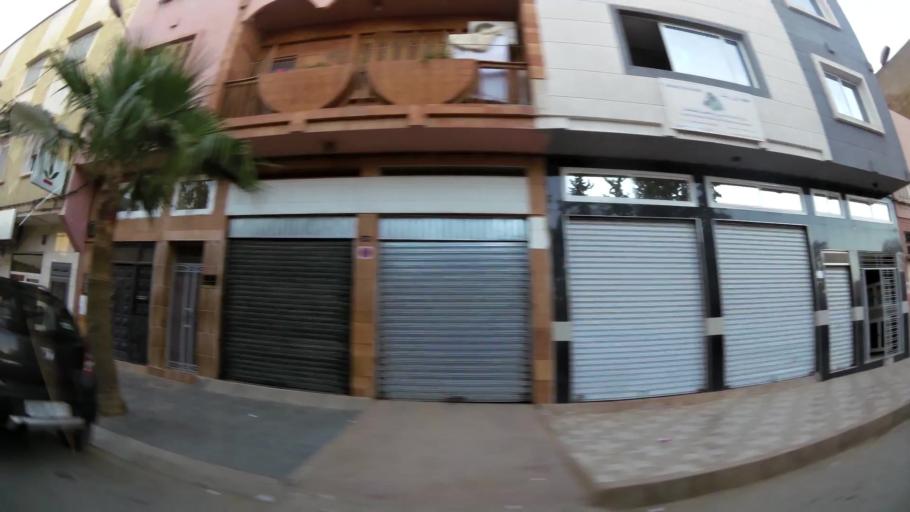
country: MA
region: Oriental
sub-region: Berkane-Taourirt
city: Berkane
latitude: 34.9229
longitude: -2.3298
